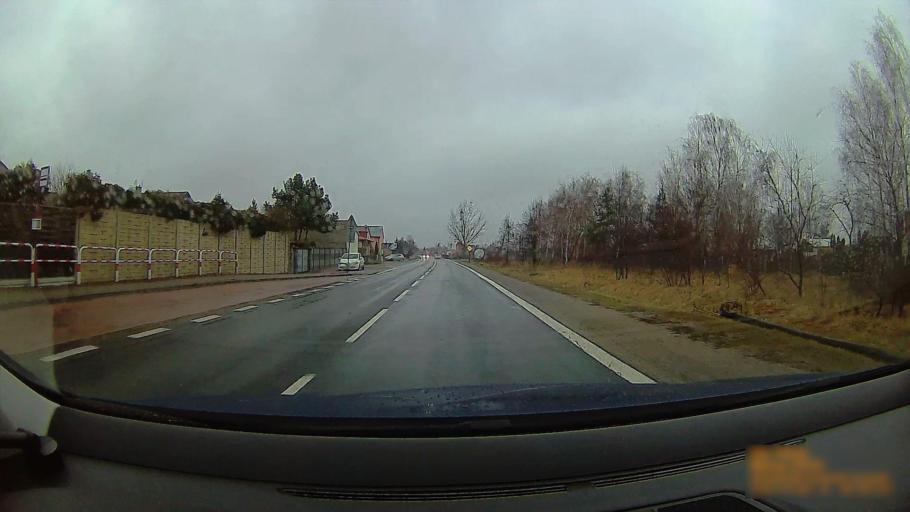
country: PL
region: Greater Poland Voivodeship
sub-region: Konin
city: Konin
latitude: 52.1838
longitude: 18.2688
